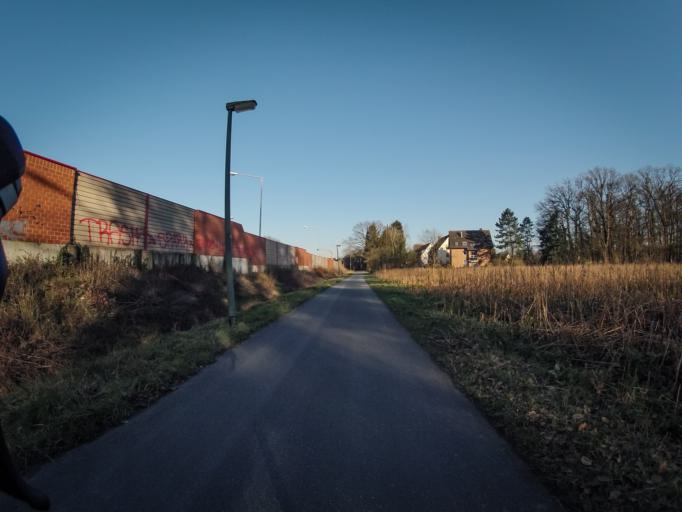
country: DE
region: Lower Saxony
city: Wallenhorst
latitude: 52.2956
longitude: 7.9875
